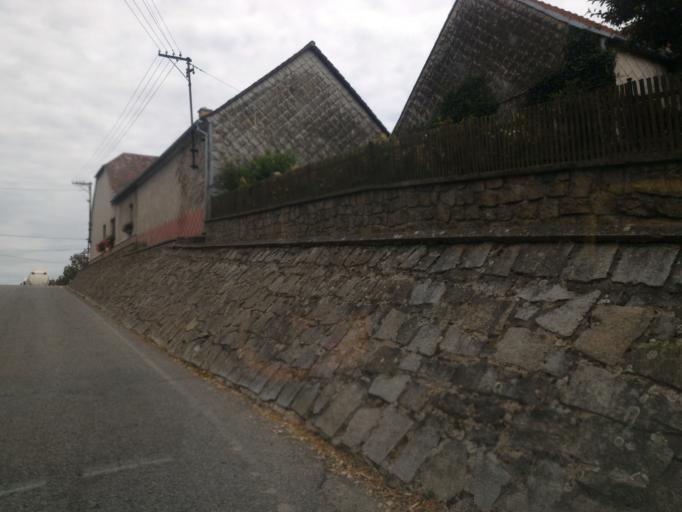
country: CZ
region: Vysocina
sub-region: Okres Jihlava
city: Telc
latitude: 49.1226
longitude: 15.5383
